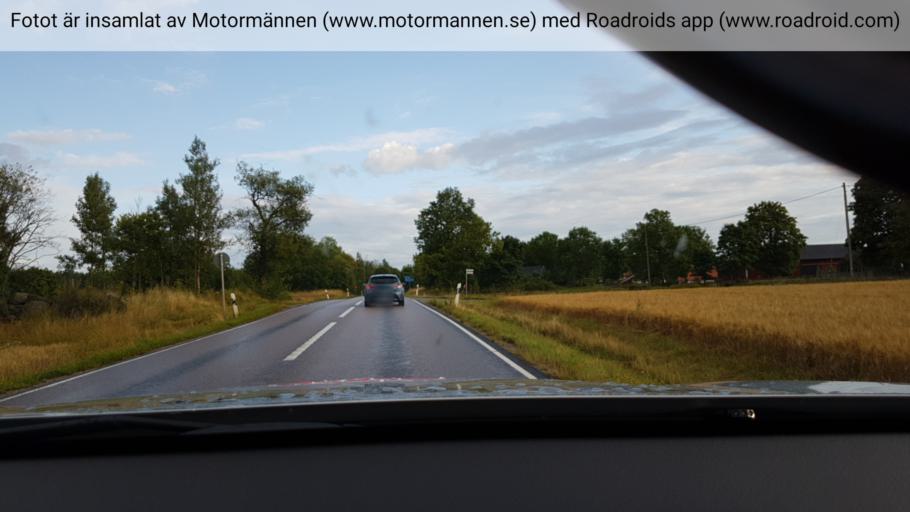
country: SE
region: Stockholm
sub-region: Norrtalje Kommun
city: Norrtalje
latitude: 59.7902
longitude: 18.6645
